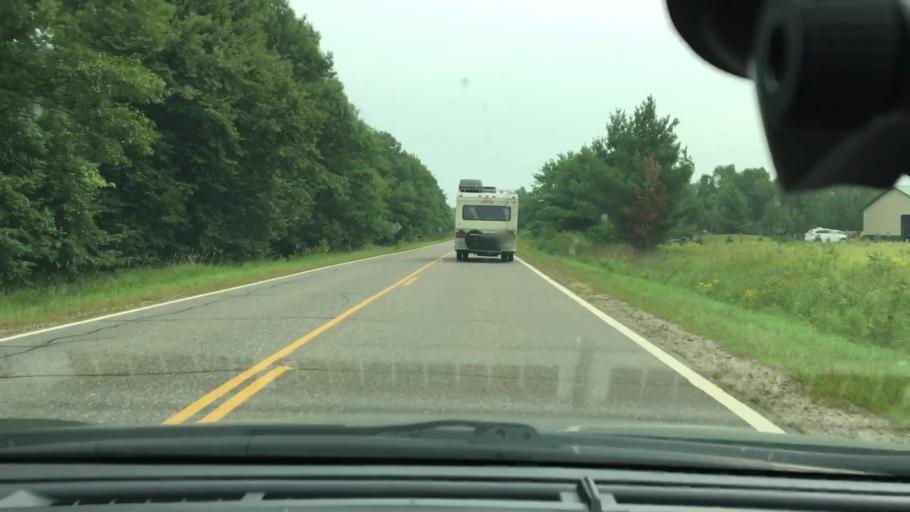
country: US
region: Minnesota
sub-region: Aitkin County
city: Aitkin
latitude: 46.4027
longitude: -93.7606
